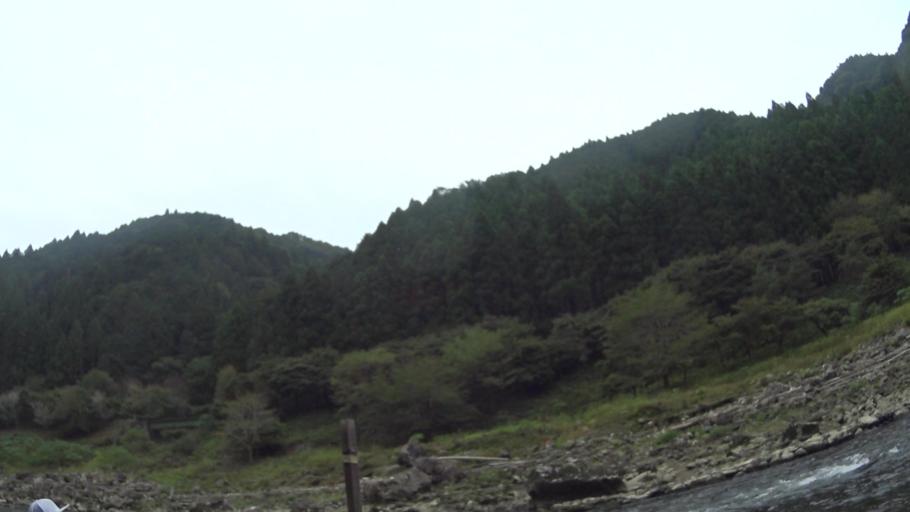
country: JP
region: Kyoto
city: Kameoka
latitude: 35.0180
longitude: 135.6334
